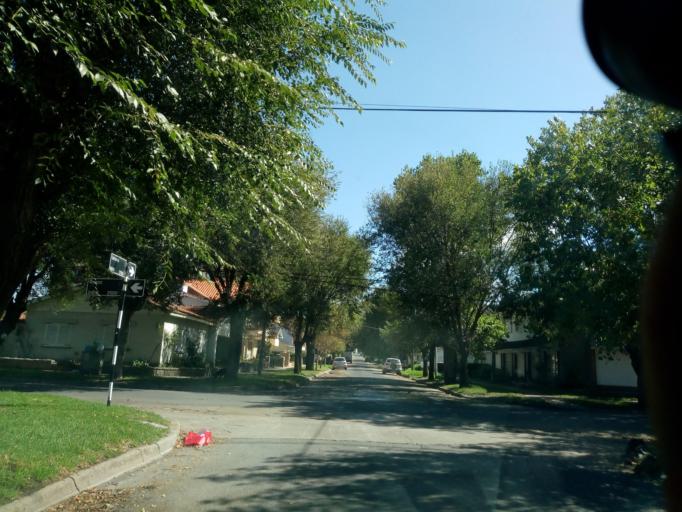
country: AR
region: Buenos Aires
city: Mar del Plata
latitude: -38.0672
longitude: -57.5488
